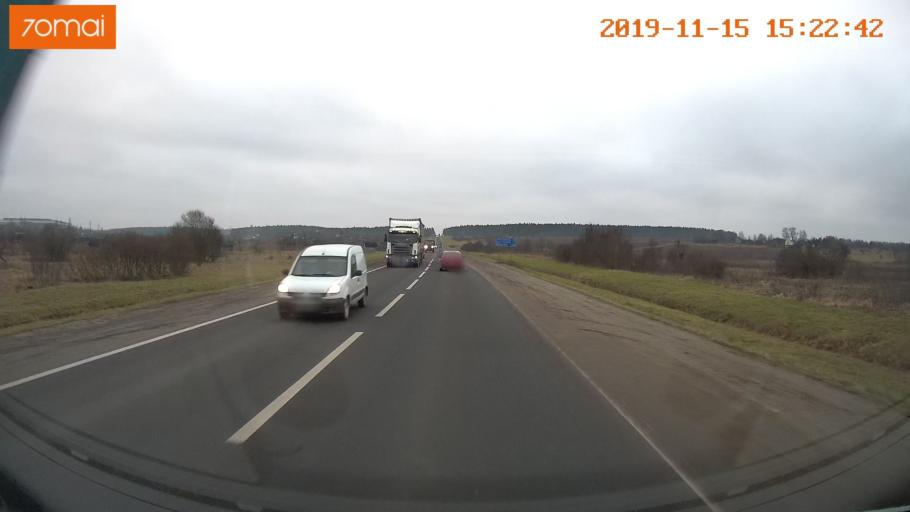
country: RU
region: Jaroslavl
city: Danilov
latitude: 58.1998
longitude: 40.1315
